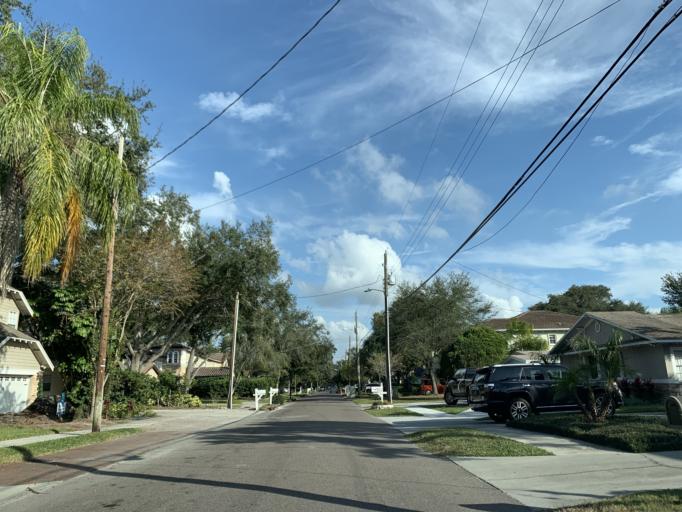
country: US
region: Florida
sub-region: Hillsborough County
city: Tampa
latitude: 27.9032
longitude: -82.5003
